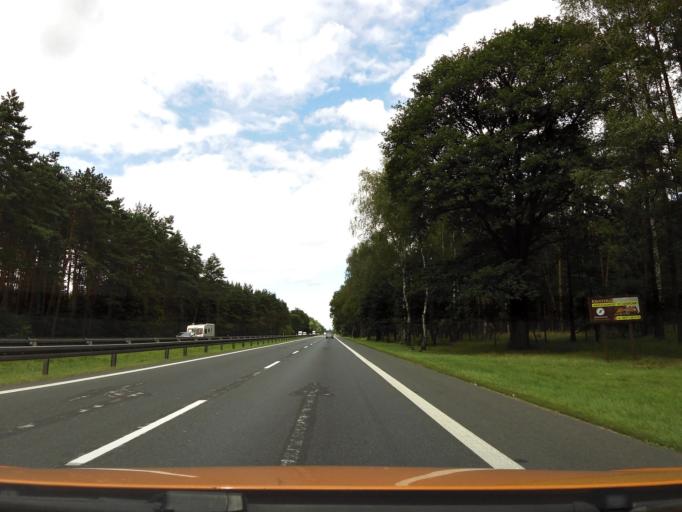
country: PL
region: West Pomeranian Voivodeship
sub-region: Powiat stargardzki
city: Kobylanka
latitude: 53.4346
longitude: 14.7761
